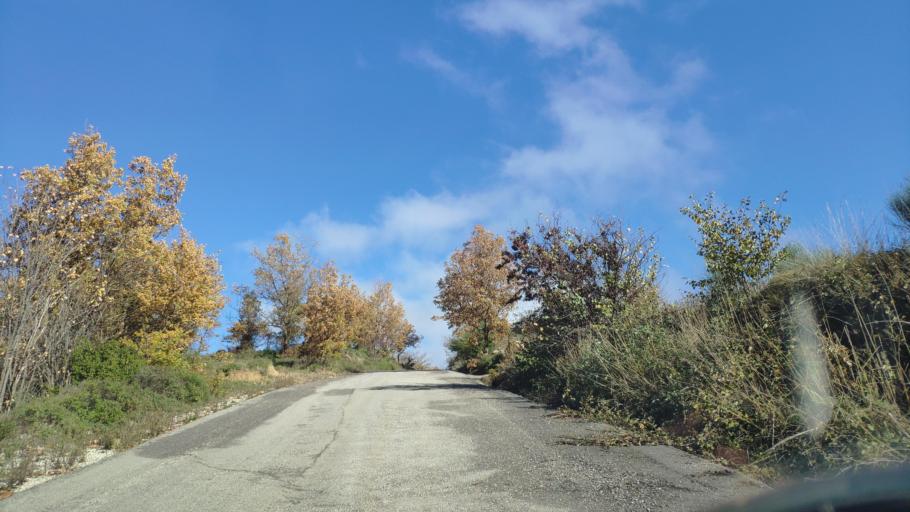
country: GR
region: West Greece
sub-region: Nomos Achaias
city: Aiyira
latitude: 38.0650
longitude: 22.4640
